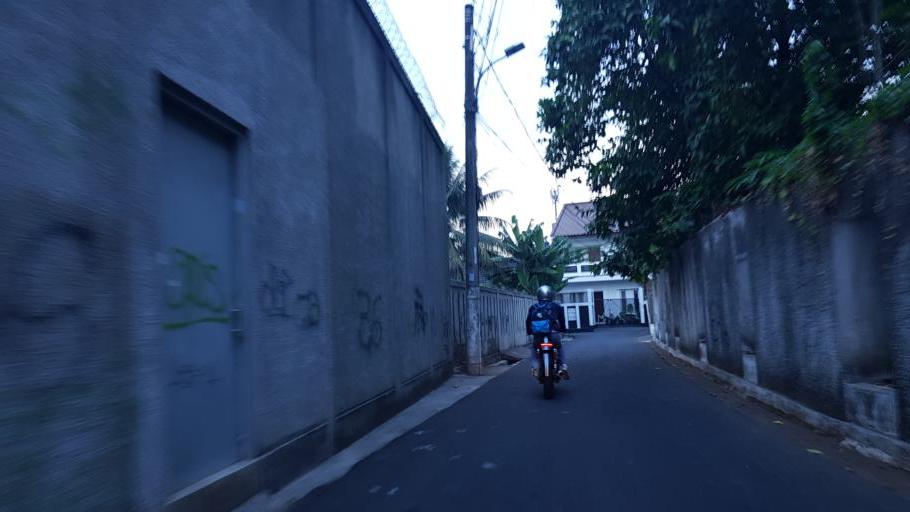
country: ID
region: West Java
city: Pamulang
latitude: -6.2976
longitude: 106.7897
